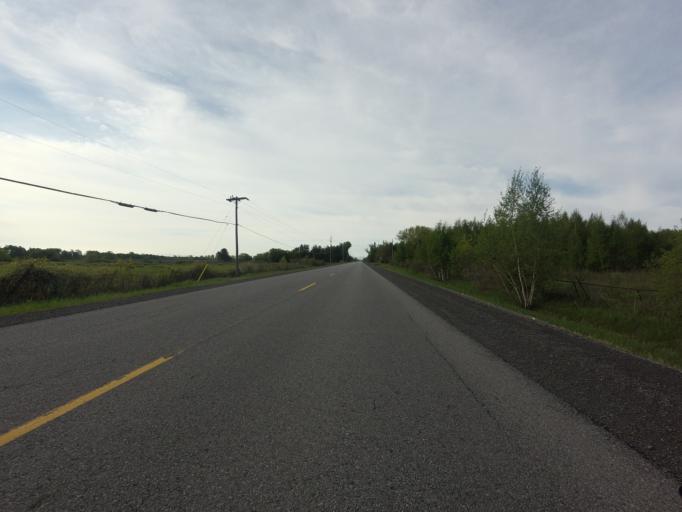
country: CA
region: Ontario
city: Ottawa
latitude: 45.3134
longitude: -75.4609
